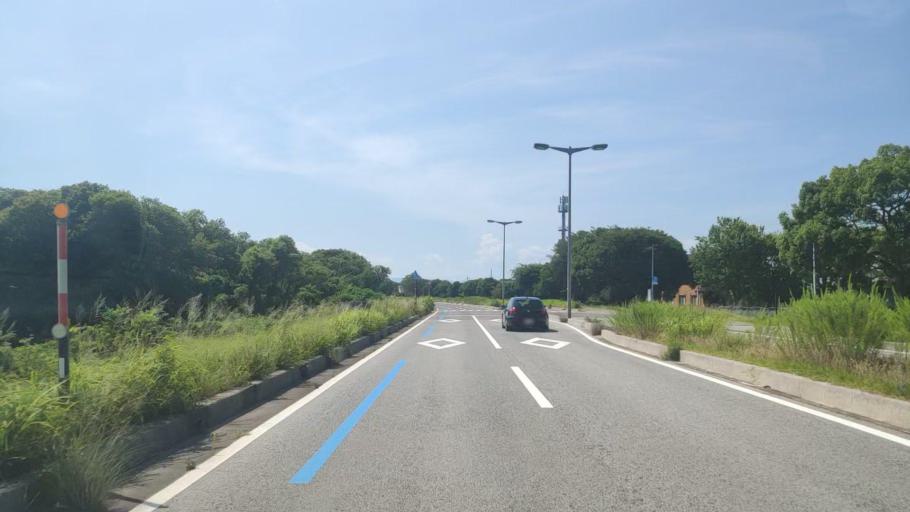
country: JP
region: Shiga Prefecture
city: Nagahama
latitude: 35.3826
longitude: 136.2542
